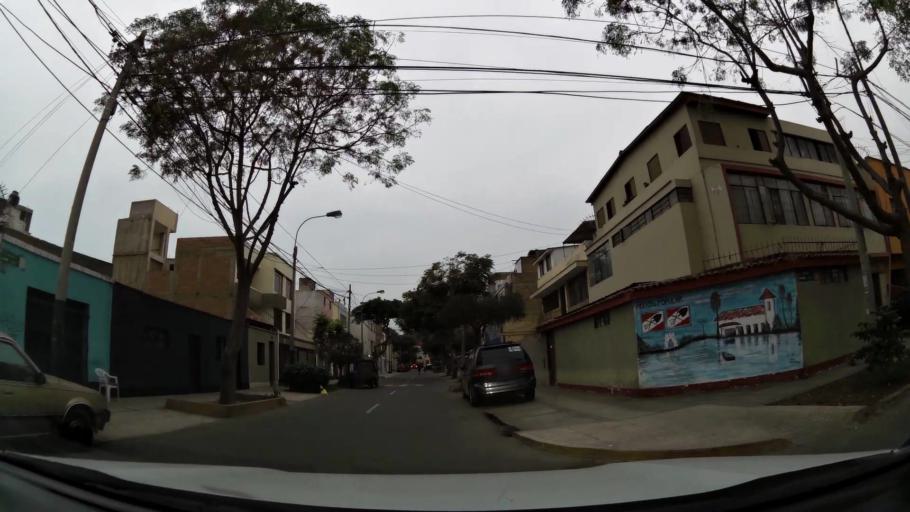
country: PE
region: Lima
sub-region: Lima
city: Surco
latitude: -12.1538
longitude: -77.0212
